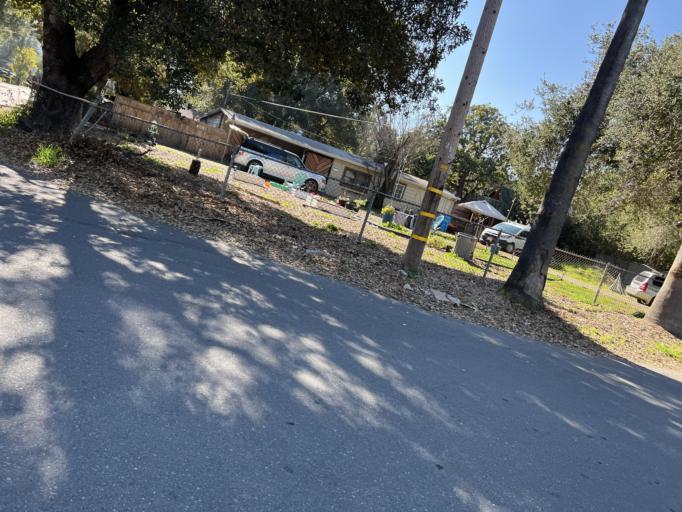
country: US
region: California
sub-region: Santa Clara County
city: Cupertino
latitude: 37.3168
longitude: -122.0651
